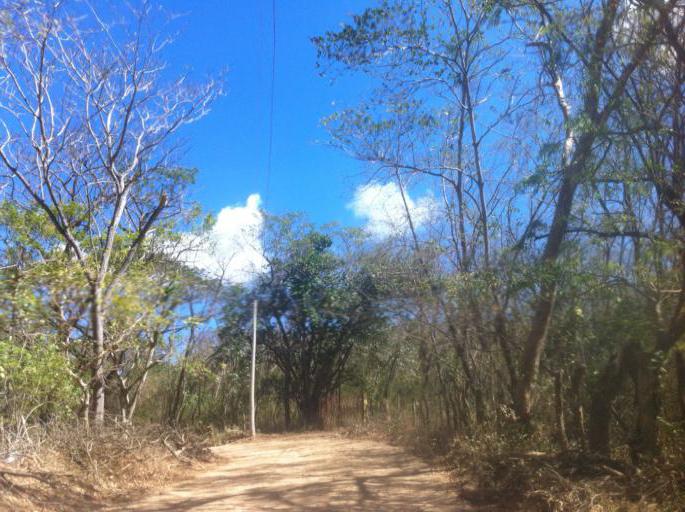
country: NI
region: Rivas
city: Tola
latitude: 11.3860
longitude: -86.0175
